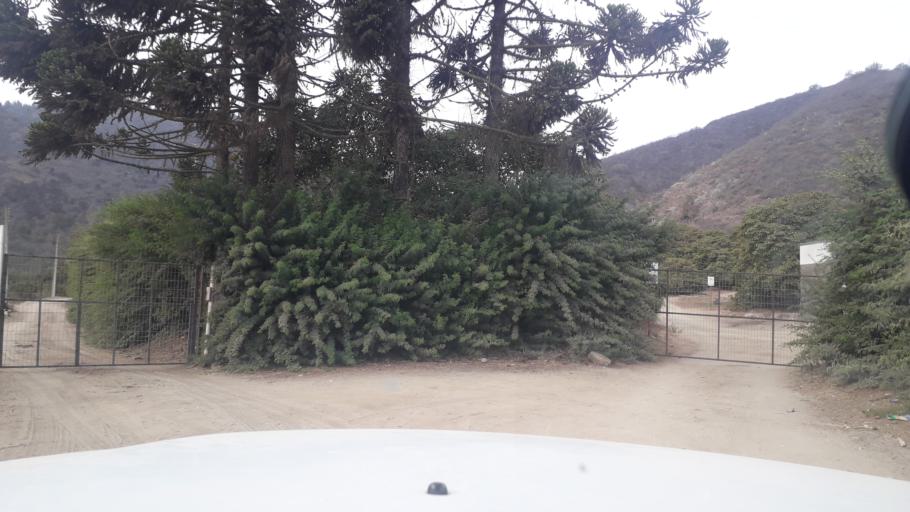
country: CL
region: Valparaiso
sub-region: Provincia de Valparaiso
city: Valparaiso
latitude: -33.1182
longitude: -71.6322
